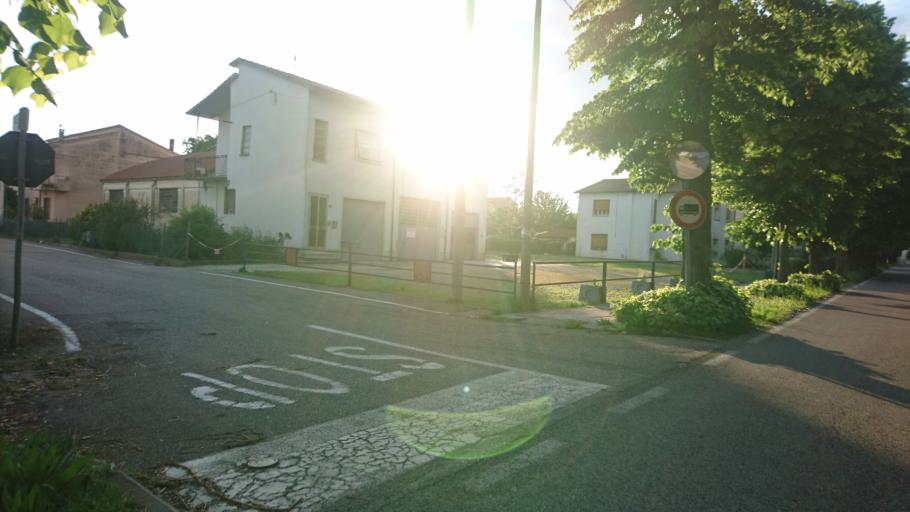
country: IT
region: Veneto
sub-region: Provincia di Rovigo
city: Ceneselli
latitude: 45.0114
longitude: 11.3716
